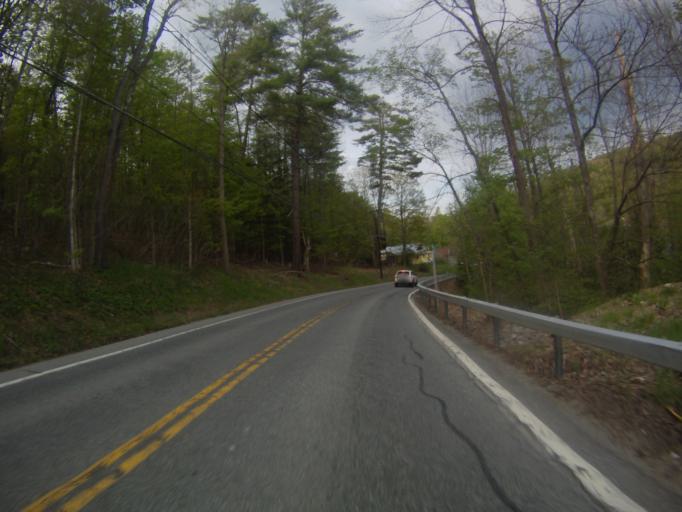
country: US
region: New York
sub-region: Warren County
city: Warrensburg
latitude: 43.6762
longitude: -73.7547
